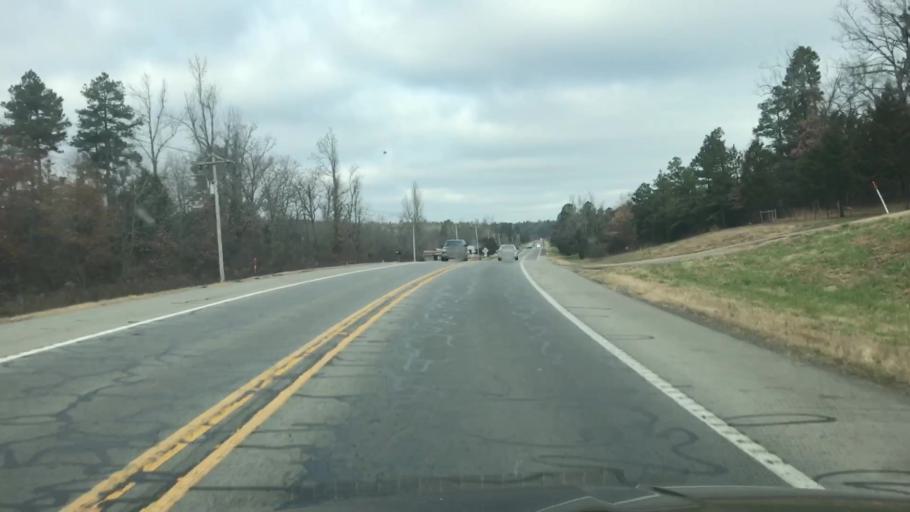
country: US
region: Arkansas
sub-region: Scott County
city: Waldron
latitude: 34.8258
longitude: -94.0382
